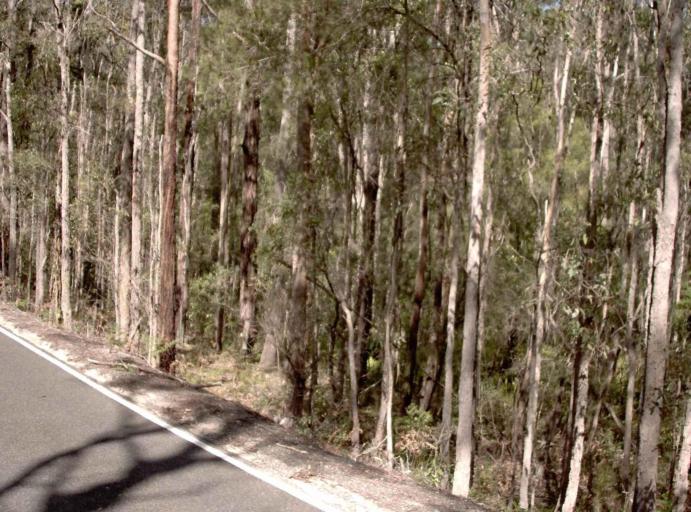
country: AU
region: New South Wales
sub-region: Bega Valley
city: Eden
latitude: -37.5328
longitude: 149.6929
